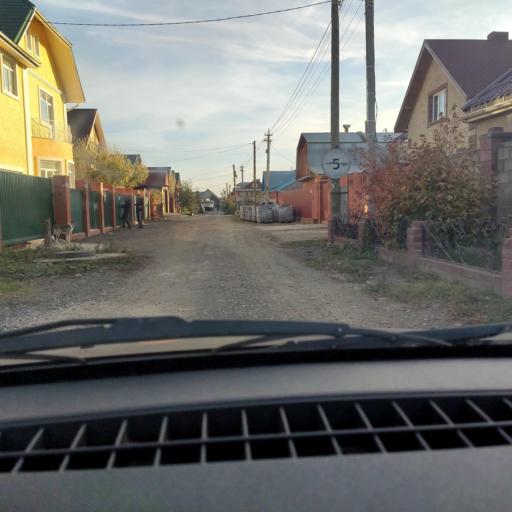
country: RU
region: Bashkortostan
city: Ufa
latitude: 54.6488
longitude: 55.9273
